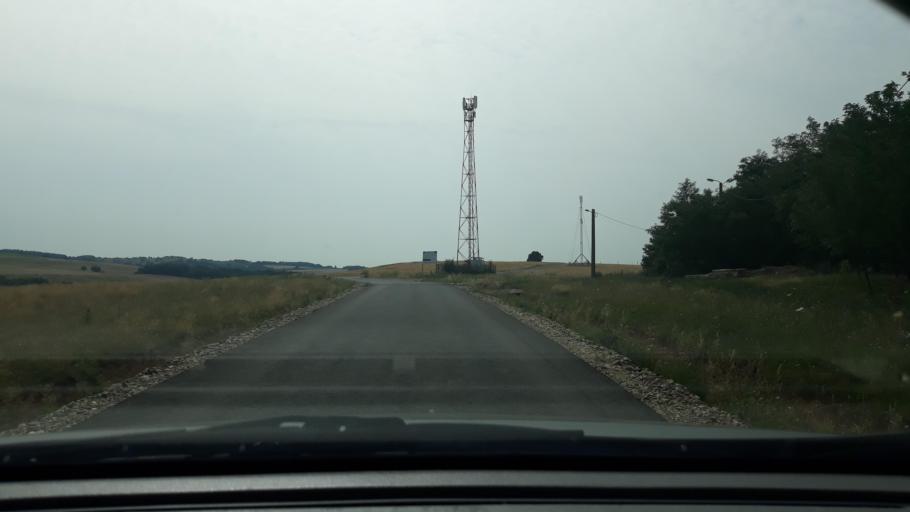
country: RO
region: Bihor
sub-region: Comuna Tauteu
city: Tauteu
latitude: 47.2659
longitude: 22.3258
